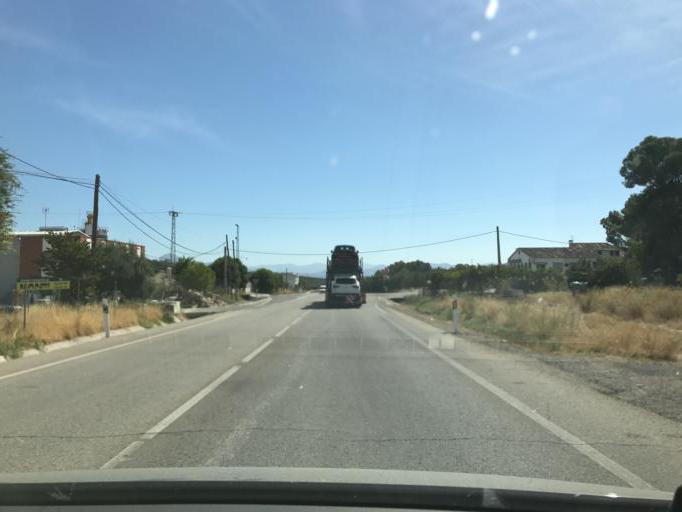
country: ES
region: Andalusia
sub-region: Province of Cordoba
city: Luque
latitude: 37.5730
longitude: -4.2603
